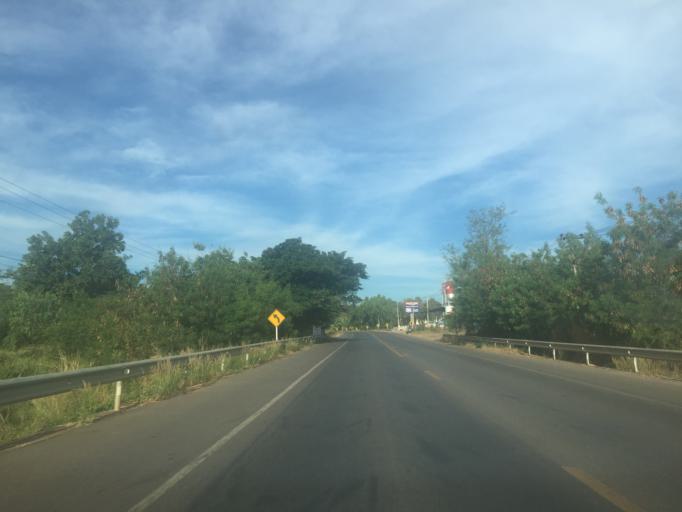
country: TH
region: Changwat Udon Thani
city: Si That
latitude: 16.9680
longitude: 103.2418
